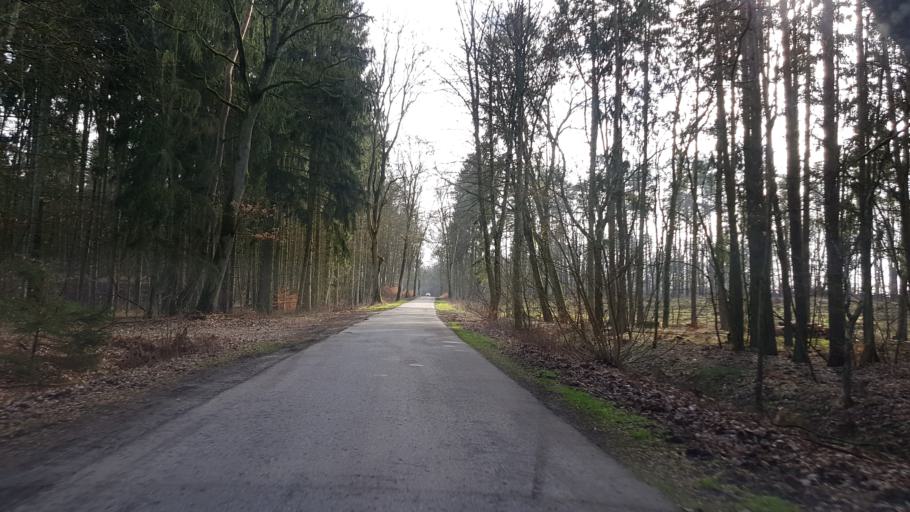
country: PL
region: West Pomeranian Voivodeship
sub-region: Powiat policki
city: Dobra
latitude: 53.5714
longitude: 14.3208
